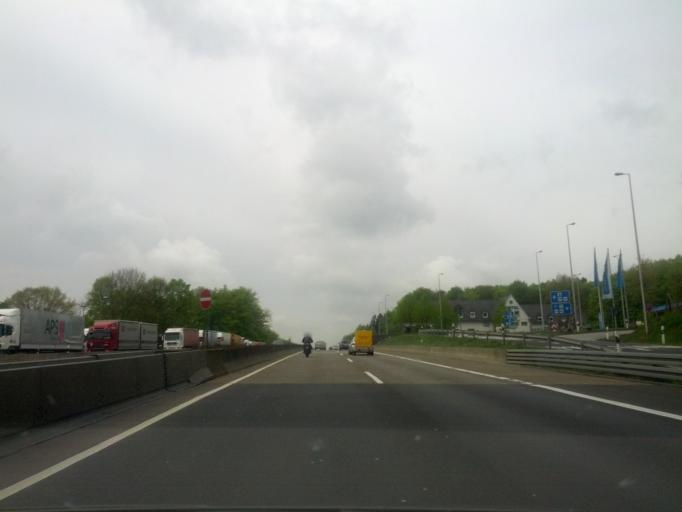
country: DE
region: Hesse
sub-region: Regierungsbezirk Giessen
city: Rabenau
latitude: 50.6238
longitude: 8.8976
